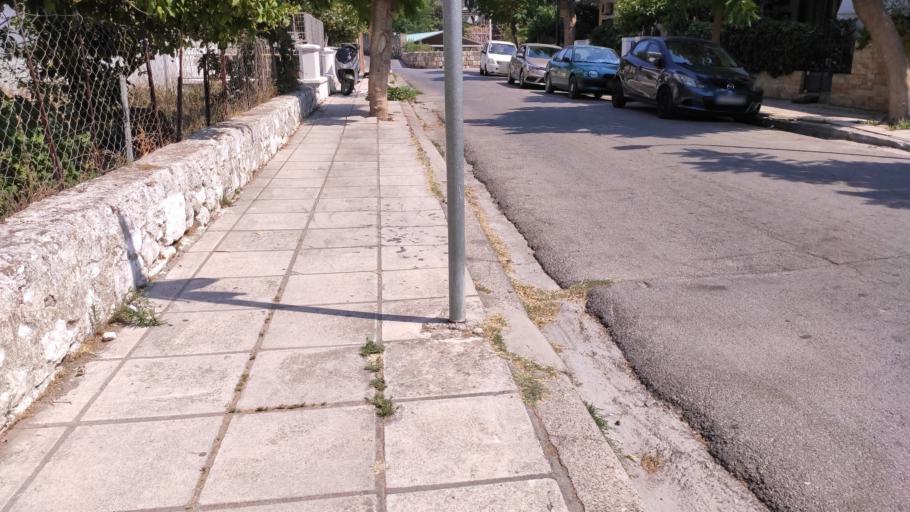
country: GR
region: South Aegean
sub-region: Nomos Dodekanisou
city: Kos
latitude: 36.8923
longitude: 27.2841
